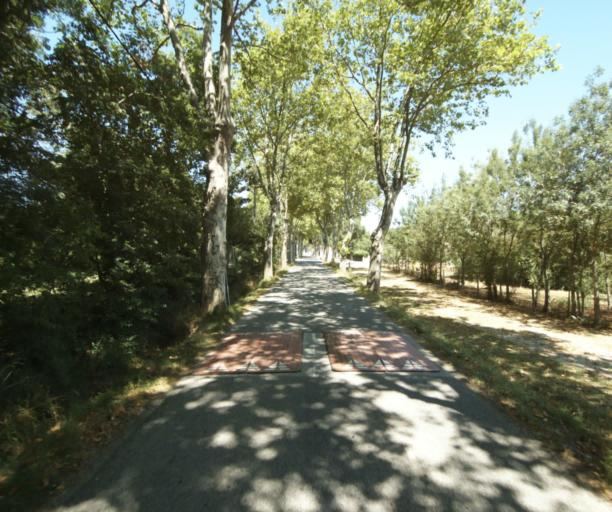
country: FR
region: Midi-Pyrenees
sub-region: Departement de la Haute-Garonne
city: Saint-Felix-Lauragais
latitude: 43.4609
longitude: 1.9285
